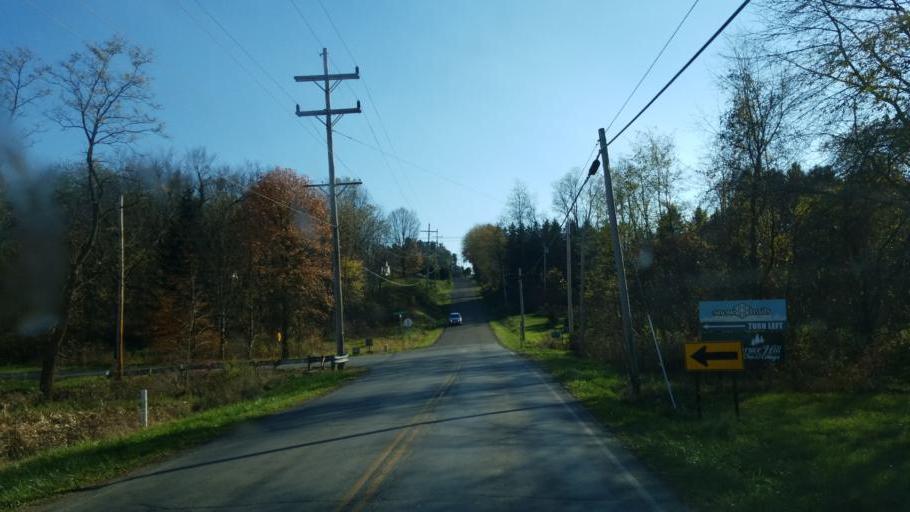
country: US
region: Ohio
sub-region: Sandusky County
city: Bellville
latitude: 40.6845
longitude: -82.5114
